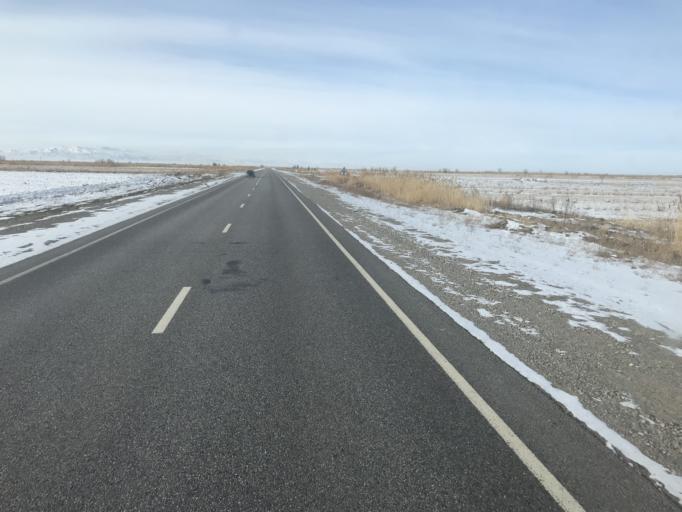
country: KZ
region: Zhambyl
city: Taraz
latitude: 43.0148
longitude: 71.3109
